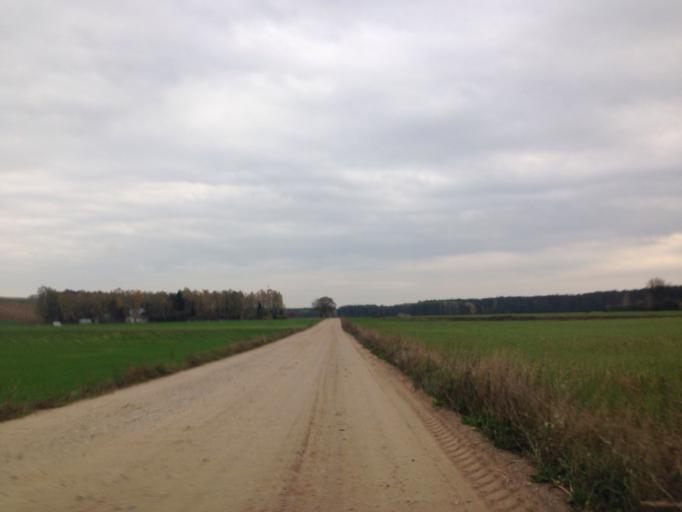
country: PL
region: Kujawsko-Pomorskie
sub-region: Powiat brodnicki
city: Brzozie
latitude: 53.2992
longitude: 19.5677
